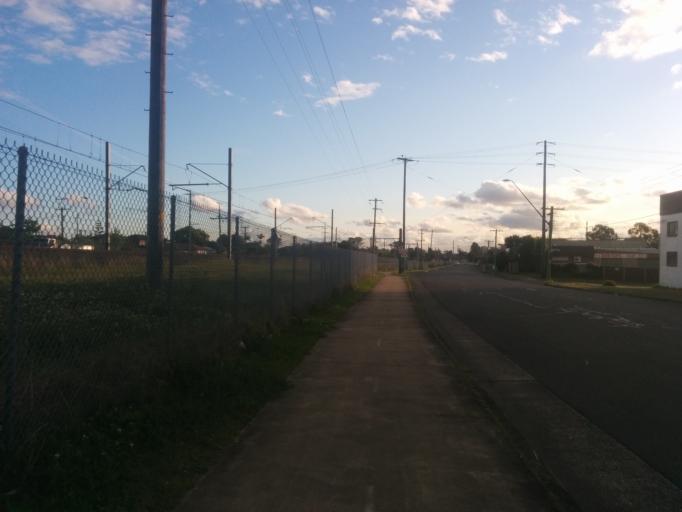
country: AU
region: New South Wales
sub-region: Holroyd
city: Guildford West
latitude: -33.8594
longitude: 150.9801
